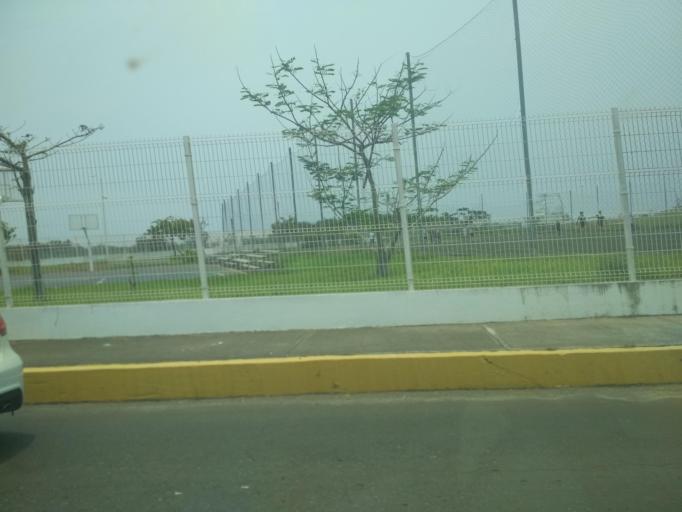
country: MX
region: Veracruz
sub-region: Alvarado
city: Playa de la Libertad
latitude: 19.0577
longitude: -96.0684
